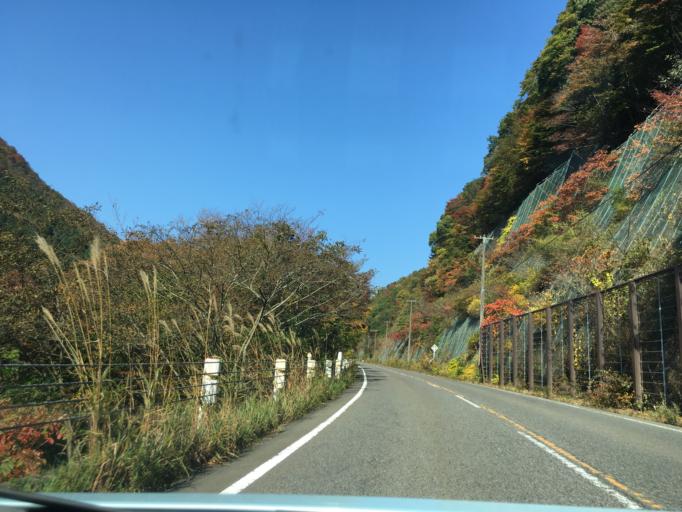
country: JP
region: Fukushima
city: Inawashiro
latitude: 37.3222
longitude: 140.1325
